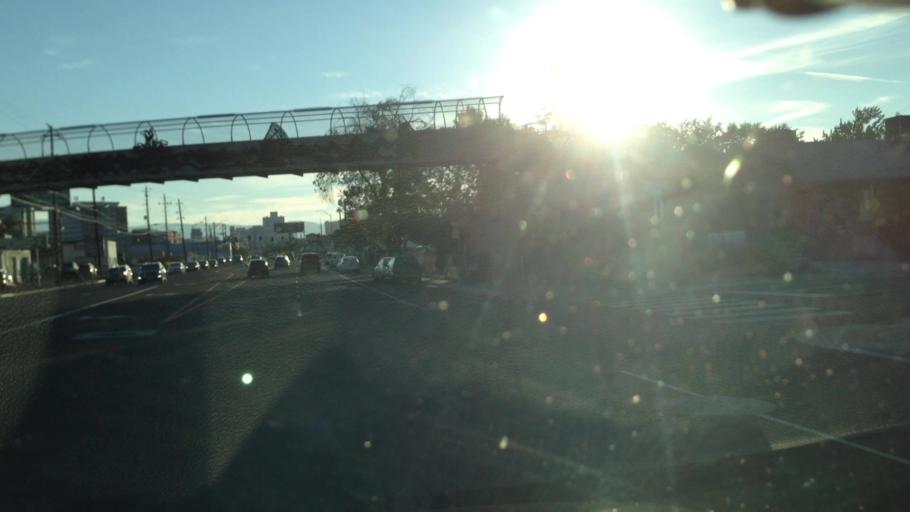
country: US
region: Nevada
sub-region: Washoe County
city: Reno
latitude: 39.5275
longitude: -119.7860
